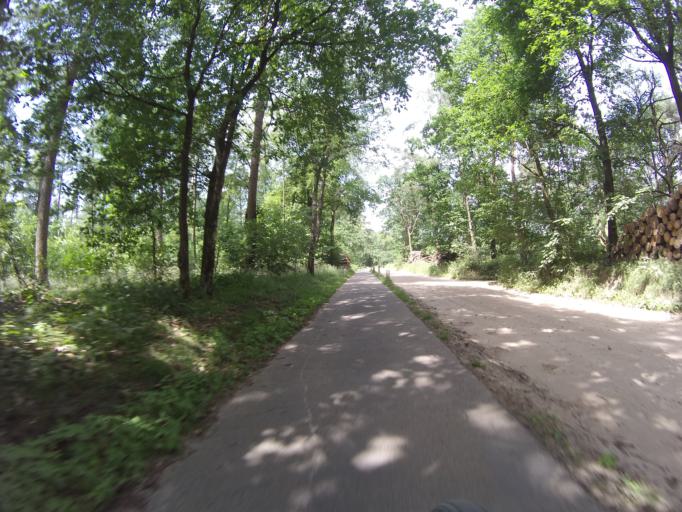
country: NL
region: Gelderland
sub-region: Gemeente Ede
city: Lunteren
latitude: 52.0907
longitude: 5.6558
